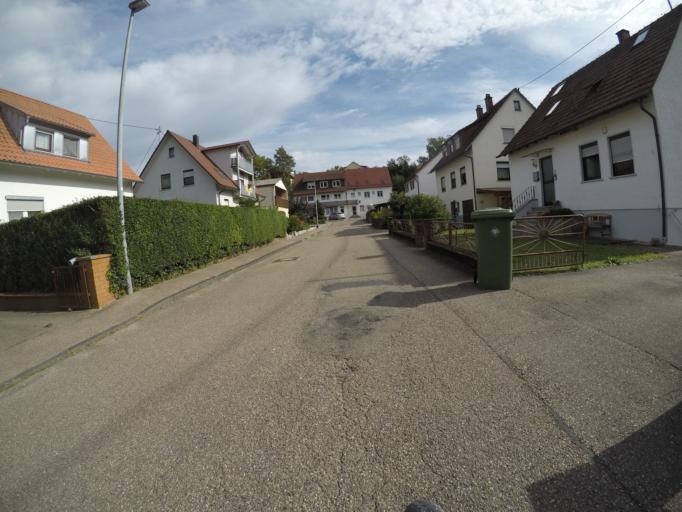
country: DE
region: Baden-Wuerttemberg
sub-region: Regierungsbezirk Stuttgart
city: Eberdingen
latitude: 48.8947
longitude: 8.9714
